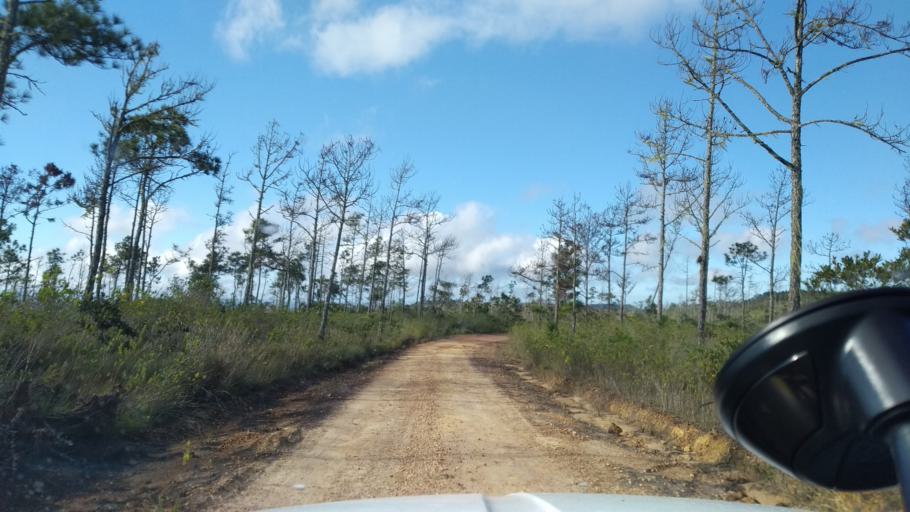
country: BZ
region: Cayo
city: Belmopan
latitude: 16.9958
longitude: -88.8353
